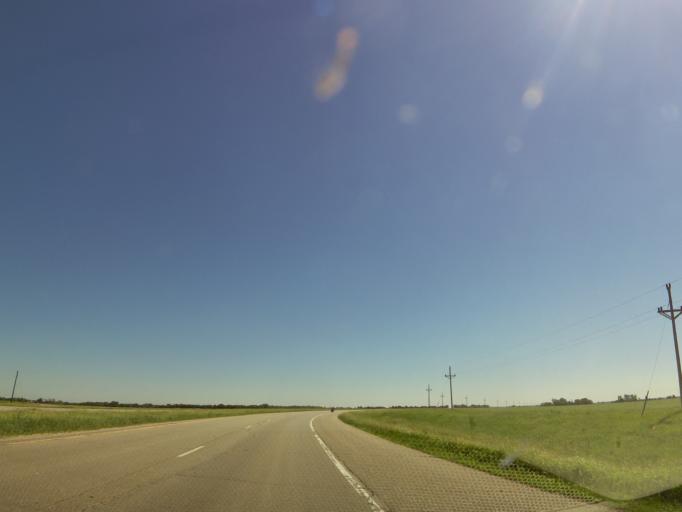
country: US
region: Minnesota
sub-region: Polk County
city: Crookston
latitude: 47.7593
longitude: -96.5454
